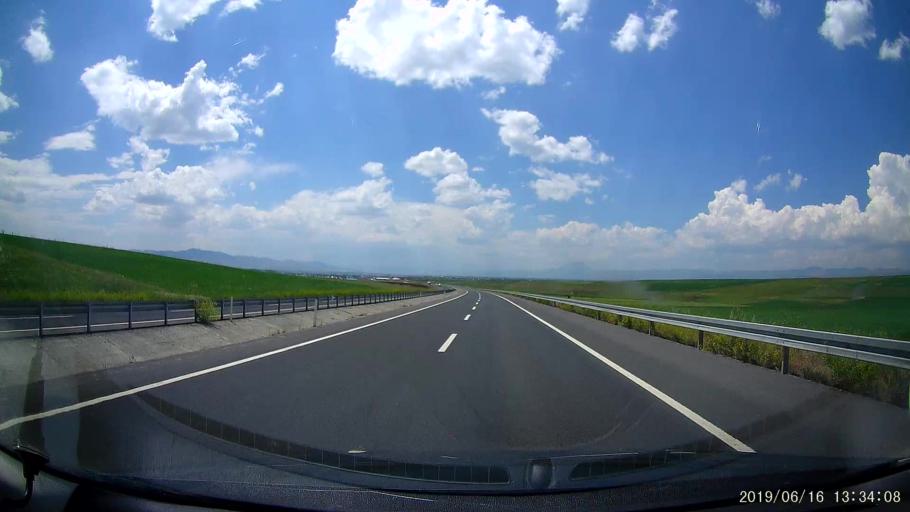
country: TR
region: Agri
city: Agri
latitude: 39.7115
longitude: 43.1352
